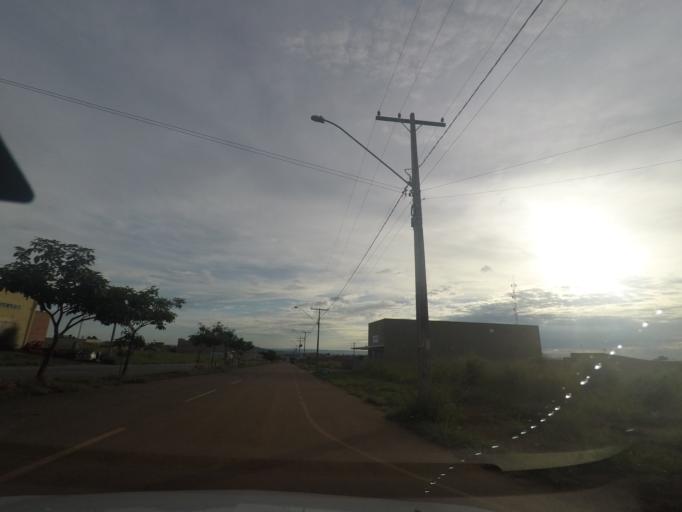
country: BR
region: Goias
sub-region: Trindade
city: Trindade
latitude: -16.7300
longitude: -49.4109
